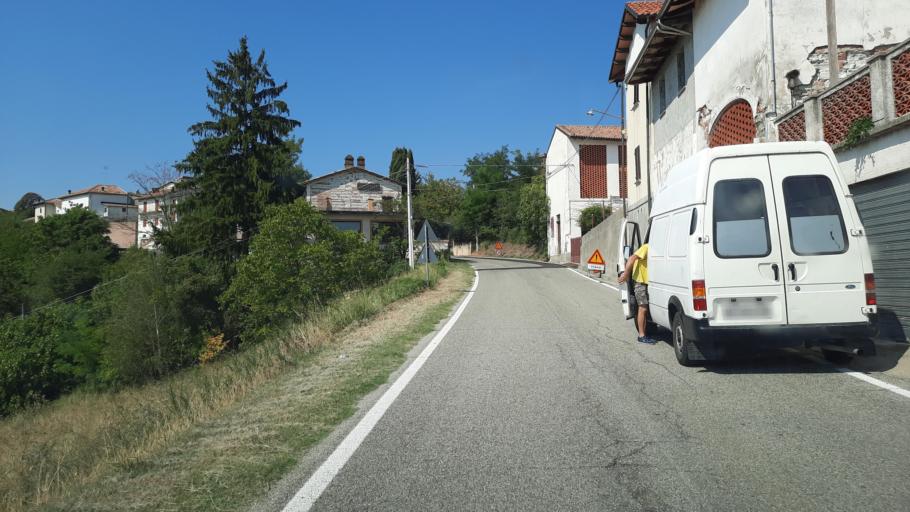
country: IT
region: Piedmont
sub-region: Provincia di Alessandria
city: Mombello Monferrato
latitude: 45.1589
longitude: 8.2454
